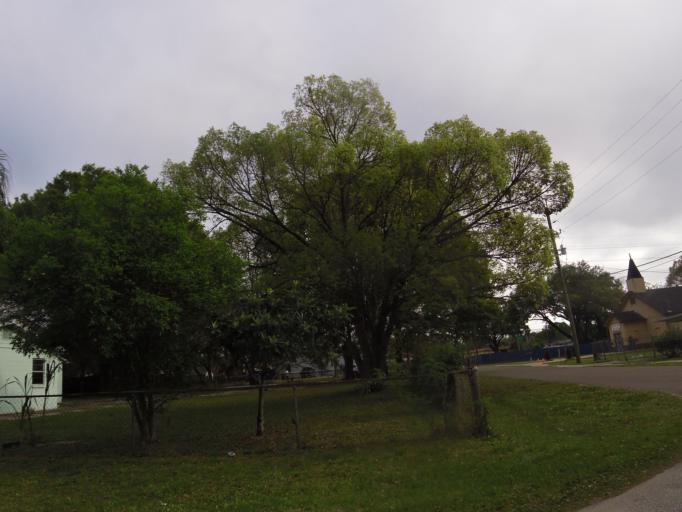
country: US
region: Florida
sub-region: Duval County
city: Jacksonville
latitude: 30.3232
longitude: -81.7190
